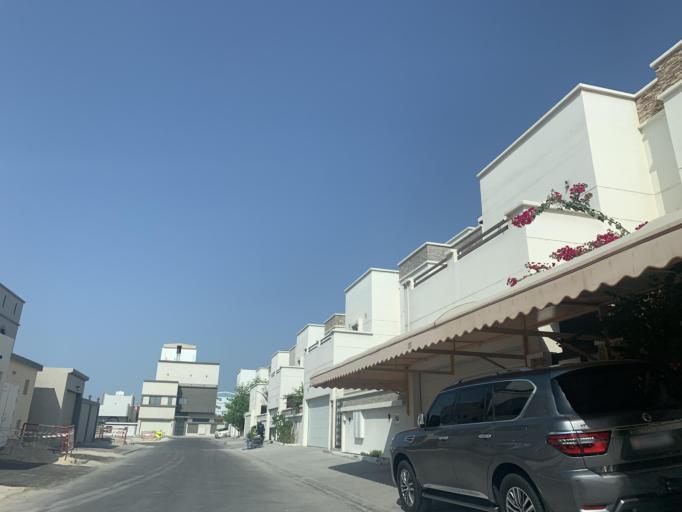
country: BH
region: Central Governorate
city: Madinat Hamad
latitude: 26.1374
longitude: 50.4921
